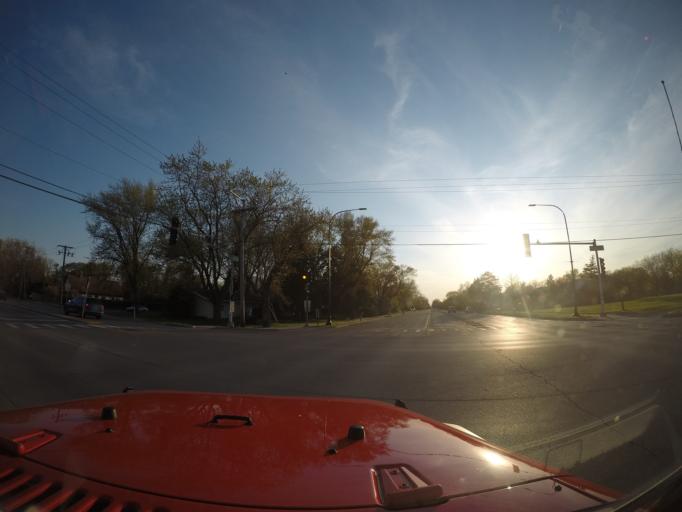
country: US
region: Illinois
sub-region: Cook County
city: Prospect Heights
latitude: 42.0880
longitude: -87.9367
